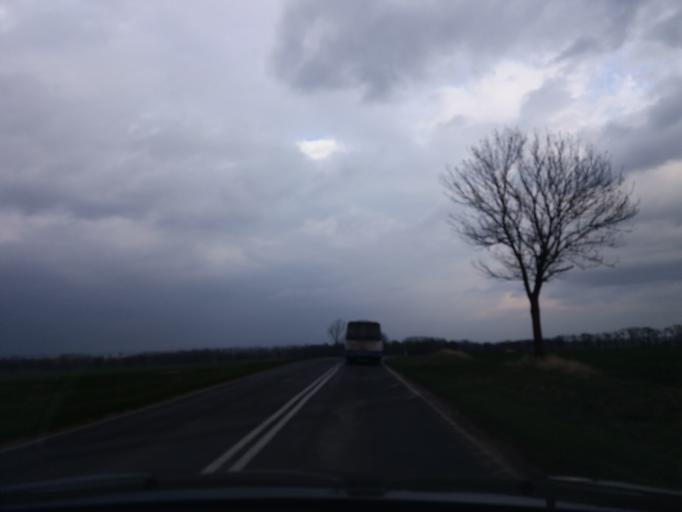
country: PL
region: West Pomeranian Voivodeship
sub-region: Powiat pyrzycki
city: Pyrzyce
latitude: 53.1368
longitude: 14.9474
